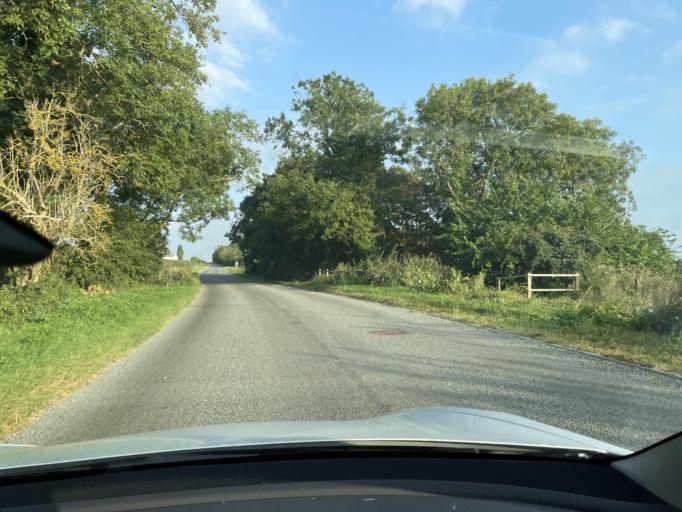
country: GB
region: England
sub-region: Bedford
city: Swineshead
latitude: 52.3684
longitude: -0.4472
